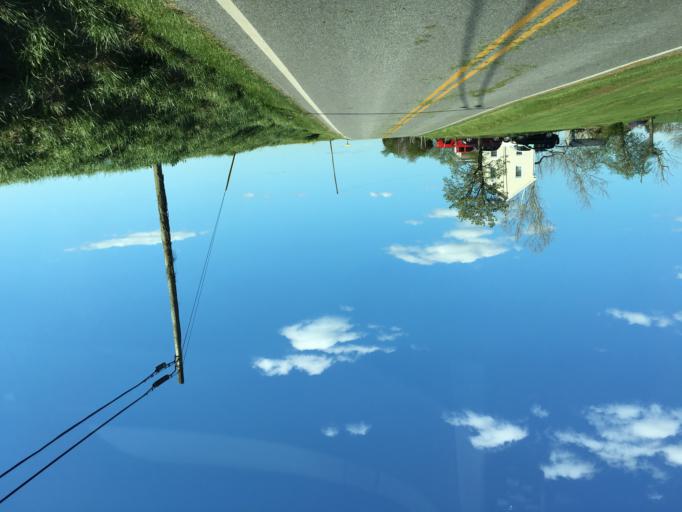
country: US
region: Maryland
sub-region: Frederick County
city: Emmitsburg
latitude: 39.6711
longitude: -77.2981
